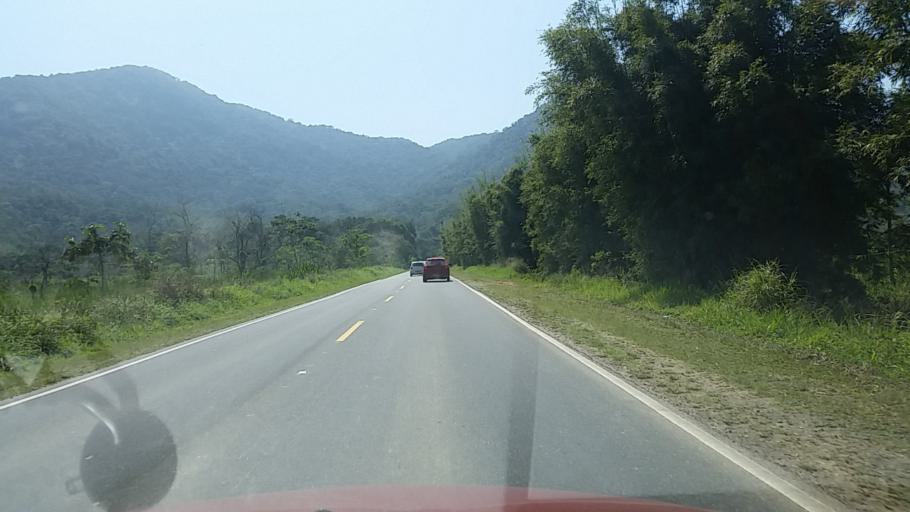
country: BR
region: Sao Paulo
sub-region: Miracatu
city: Miracatu
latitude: -24.3826
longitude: -47.5233
